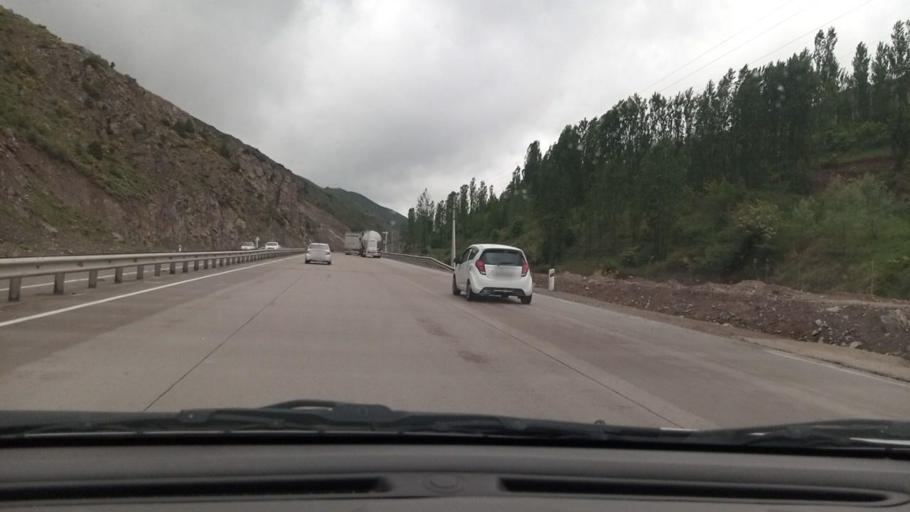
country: UZ
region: Toshkent
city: Angren
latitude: 41.0456
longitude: 70.5731
